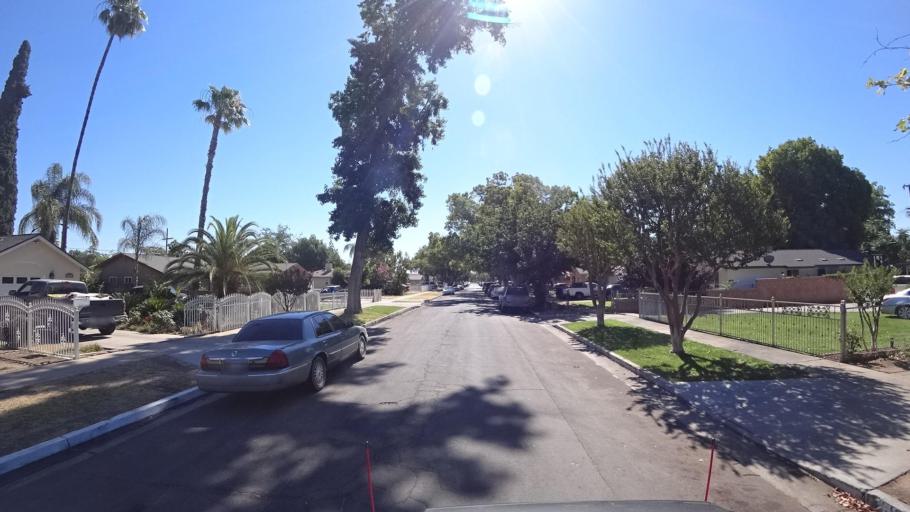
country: US
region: California
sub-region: Fresno County
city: Fresno
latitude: 36.7813
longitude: -119.7947
